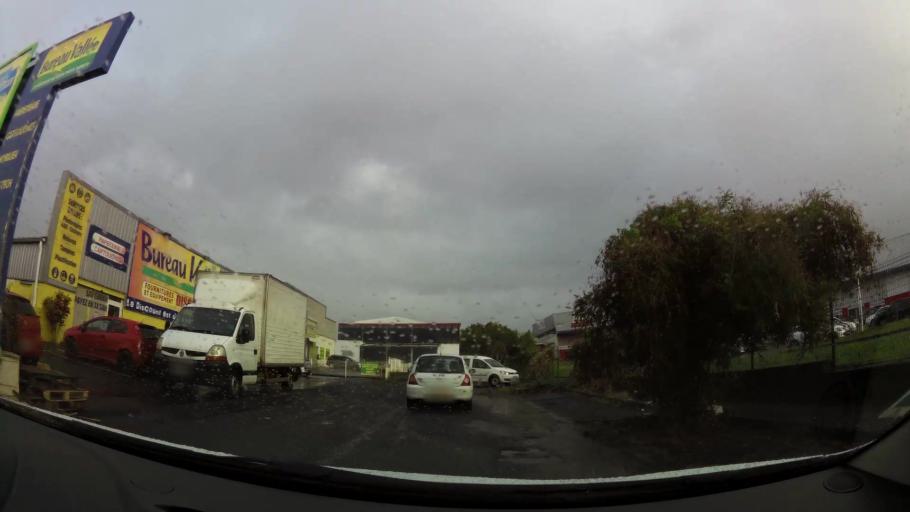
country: RE
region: Reunion
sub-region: Reunion
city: Saint-Andre
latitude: -20.9611
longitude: 55.6600
